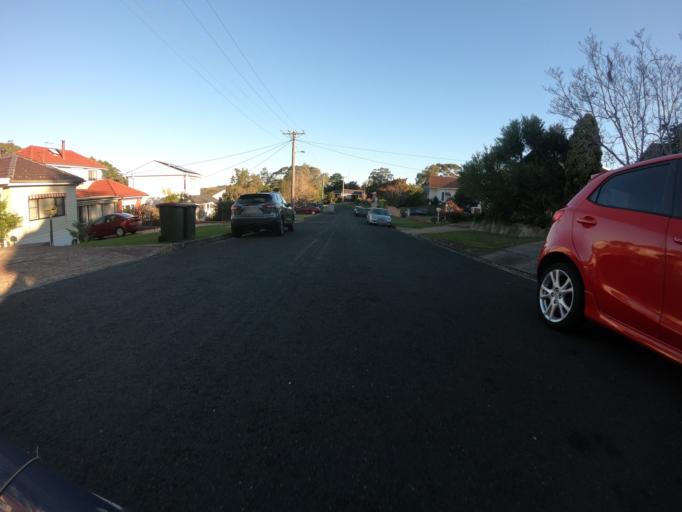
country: AU
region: New South Wales
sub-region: Wollongong
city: West Wollongong
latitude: -34.4326
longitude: 150.8550
